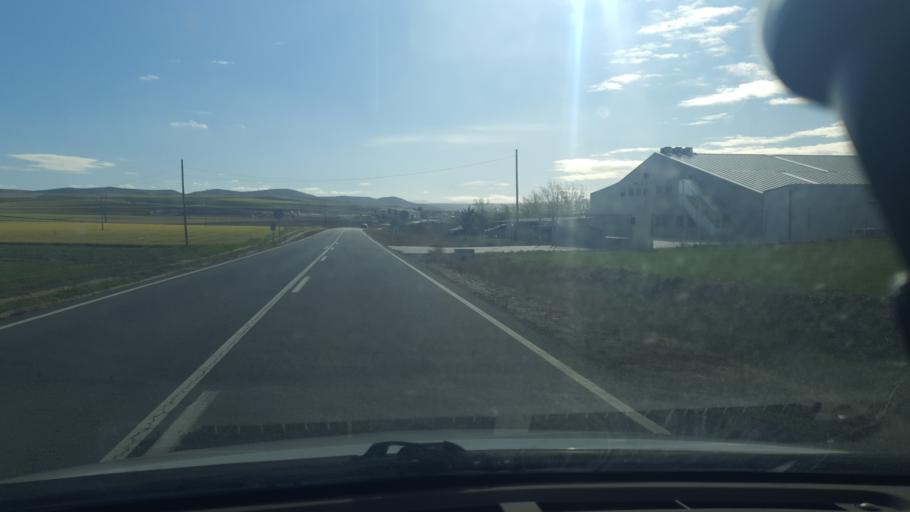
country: ES
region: Castille and Leon
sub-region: Provincia de Avila
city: Gotarrendura
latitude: 40.8087
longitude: -4.7571
